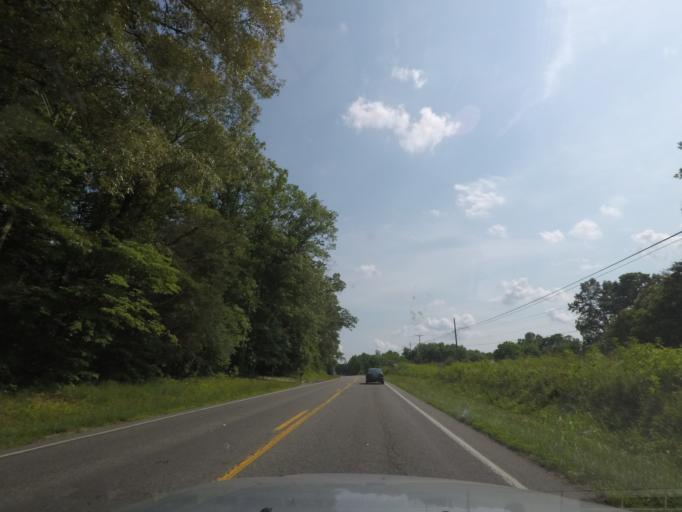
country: US
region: Virginia
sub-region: Fluvanna County
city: Weber City
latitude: 37.7967
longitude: -78.2401
